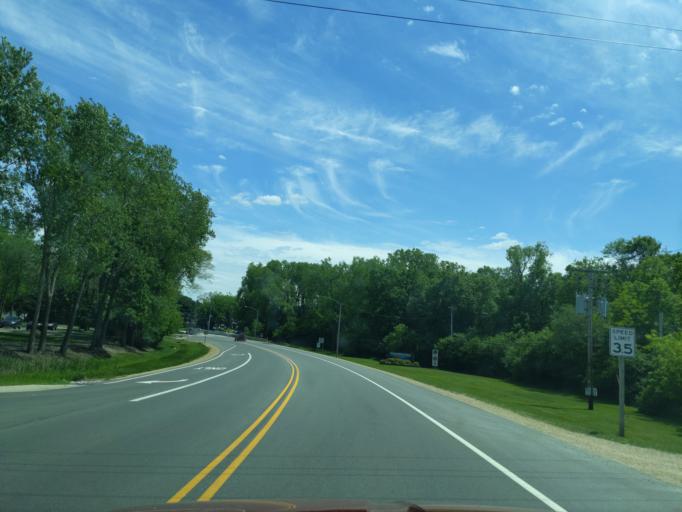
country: US
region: Wisconsin
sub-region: Columbia County
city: Pardeeville
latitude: 43.5468
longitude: -89.3058
